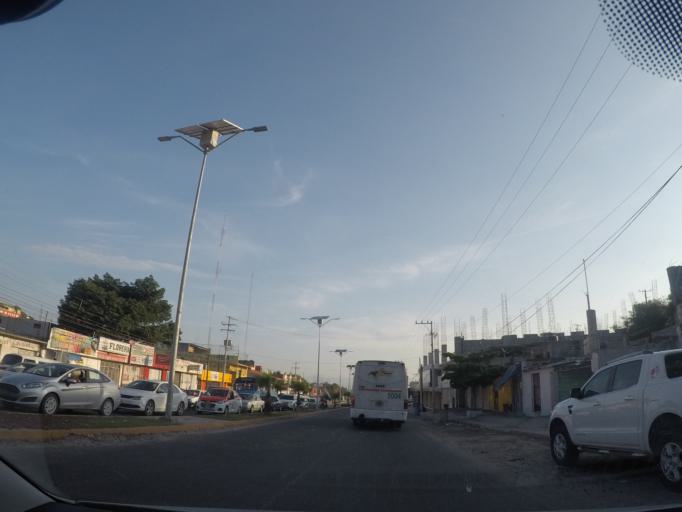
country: MX
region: Oaxaca
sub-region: Salina Cruz
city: Salina Cruz
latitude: 16.1971
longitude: -95.2017
